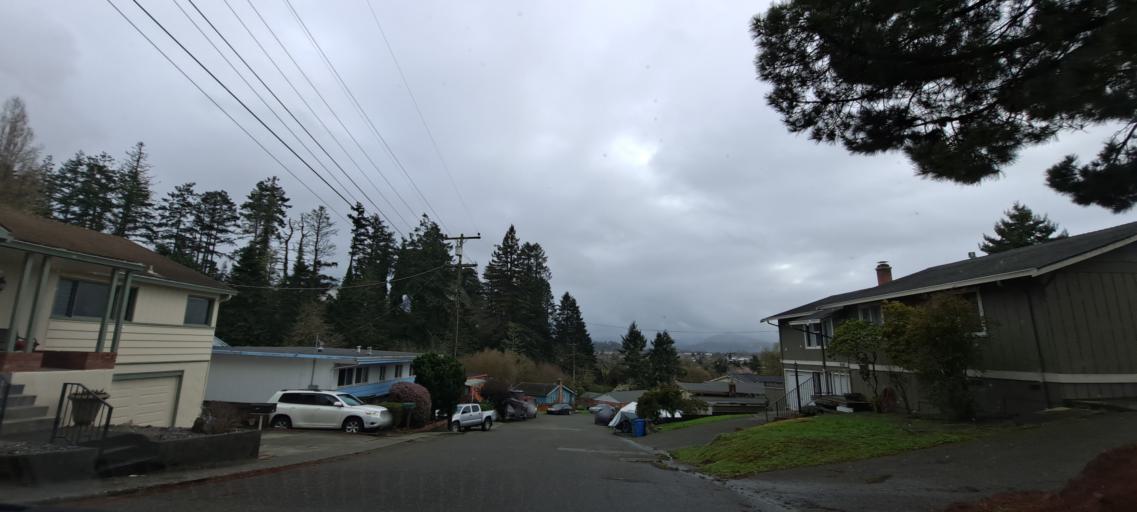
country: US
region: California
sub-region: Humboldt County
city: Fortuna
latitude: 40.5982
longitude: -124.1434
